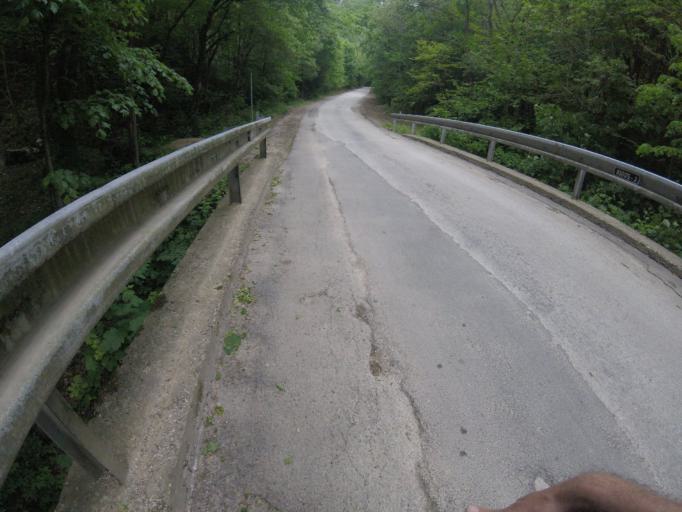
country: SK
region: Kosicky
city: Medzev
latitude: 48.6424
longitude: 20.8479
